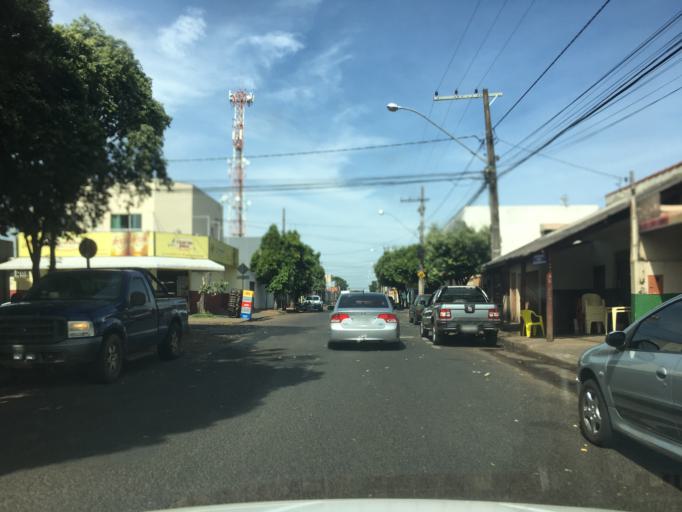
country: BR
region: Minas Gerais
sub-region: Uberlandia
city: Uberlandia
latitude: -18.9388
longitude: -48.3154
